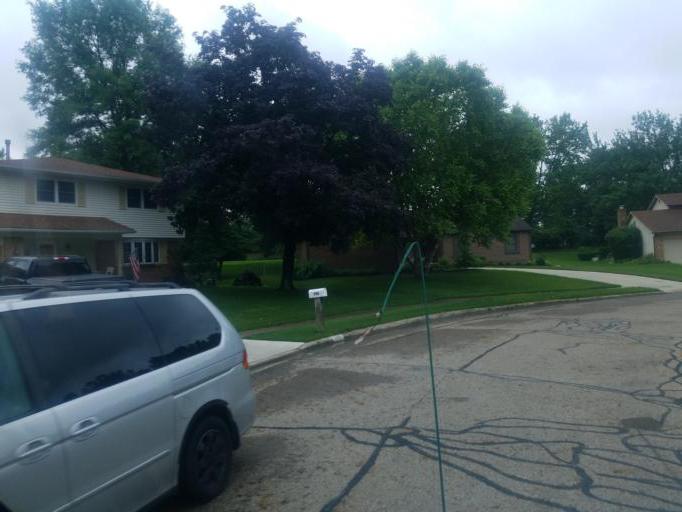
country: US
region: Ohio
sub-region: Franklin County
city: Gahanna
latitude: 40.0165
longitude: -82.8556
